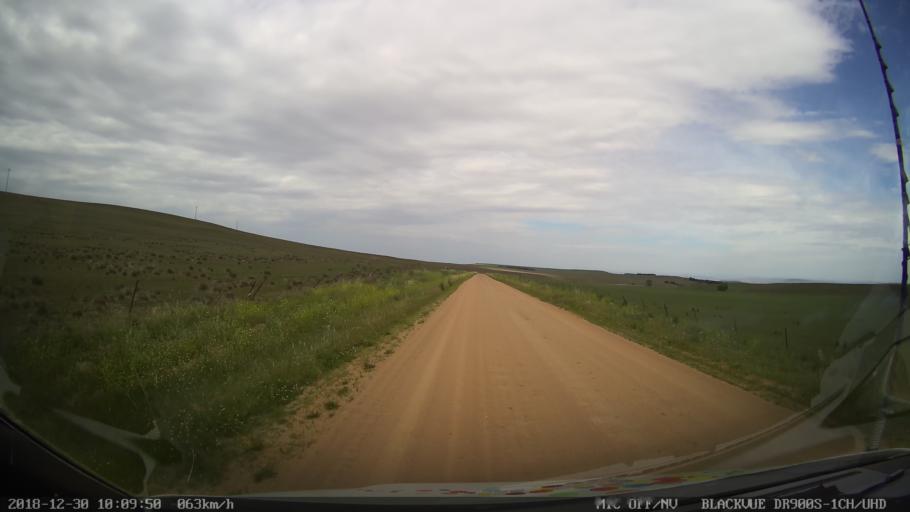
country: AU
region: New South Wales
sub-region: Cooma-Monaro
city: Cooma
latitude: -36.5496
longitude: 149.1013
